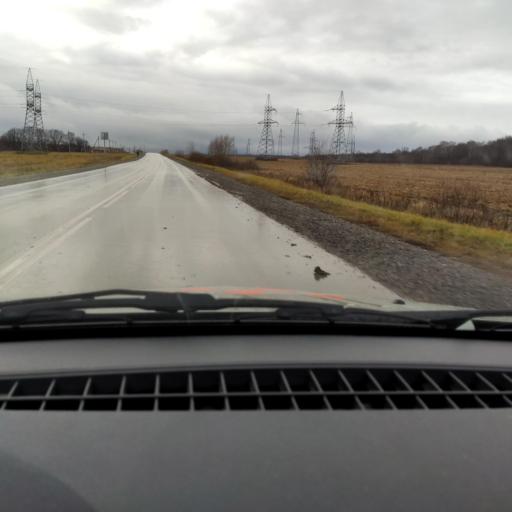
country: RU
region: Bashkortostan
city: Mikhaylovka
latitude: 54.8325
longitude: 55.9263
